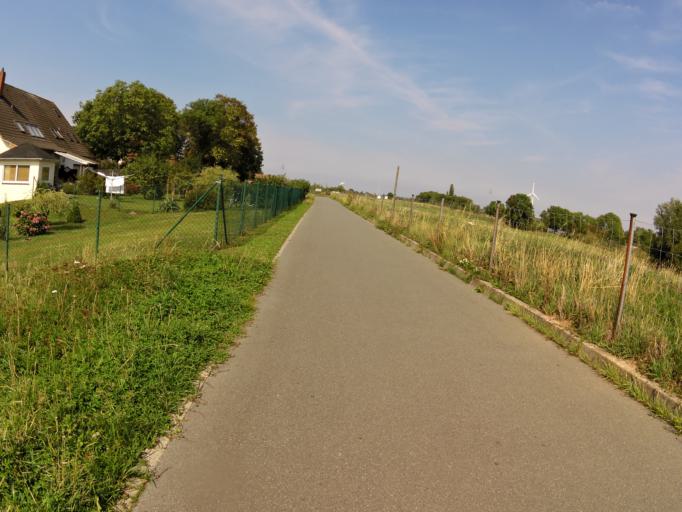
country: DE
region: Lower Saxony
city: Riede
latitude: 53.0126
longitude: 8.8888
